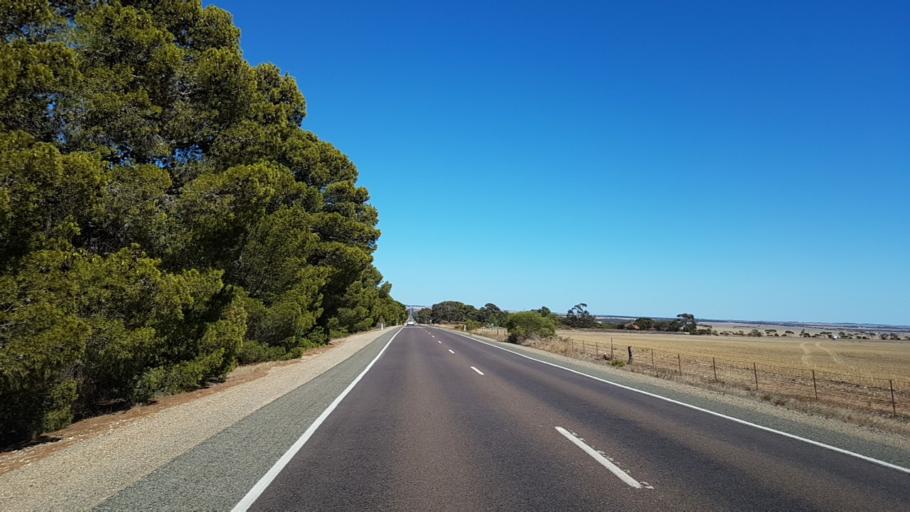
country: AU
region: South Australia
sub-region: Copper Coast
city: Kadina
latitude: -34.0588
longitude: 138.0314
